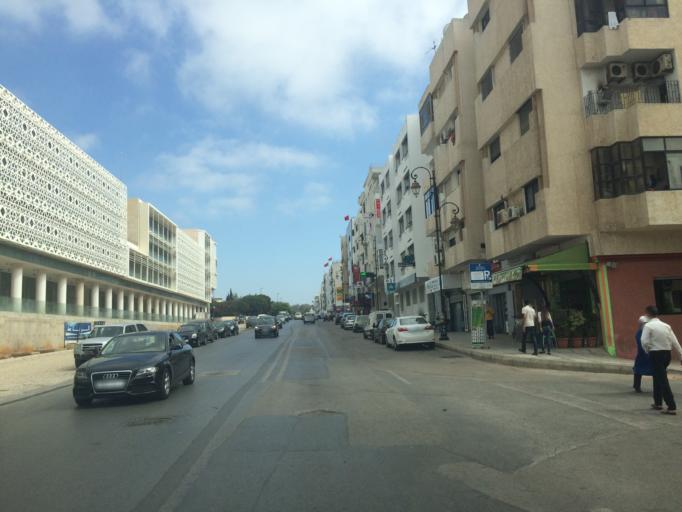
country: MA
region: Rabat-Sale-Zemmour-Zaer
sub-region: Rabat
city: Rabat
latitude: 34.0033
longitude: -6.8462
